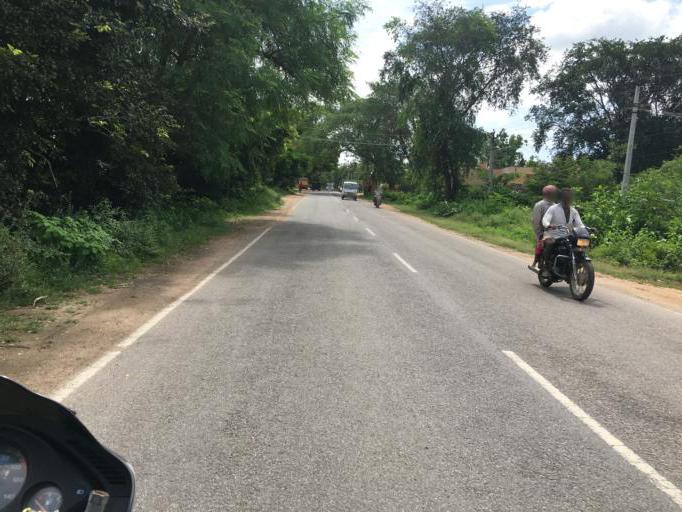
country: IN
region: Telangana
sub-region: Nalgonda
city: Nalgonda
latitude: 17.1673
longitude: 79.4118
